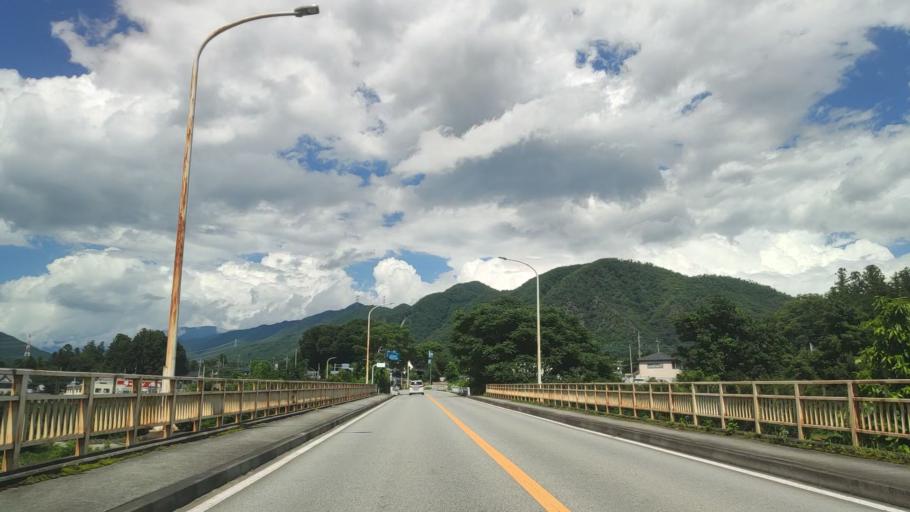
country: JP
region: Yamanashi
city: Enzan
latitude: 35.7305
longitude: 138.7106
